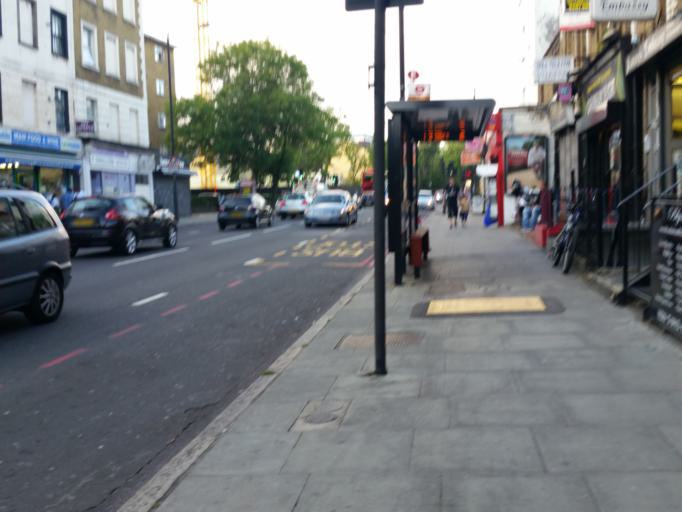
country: GB
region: England
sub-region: Greater London
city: Camden Town
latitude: 51.5421
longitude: -0.1379
